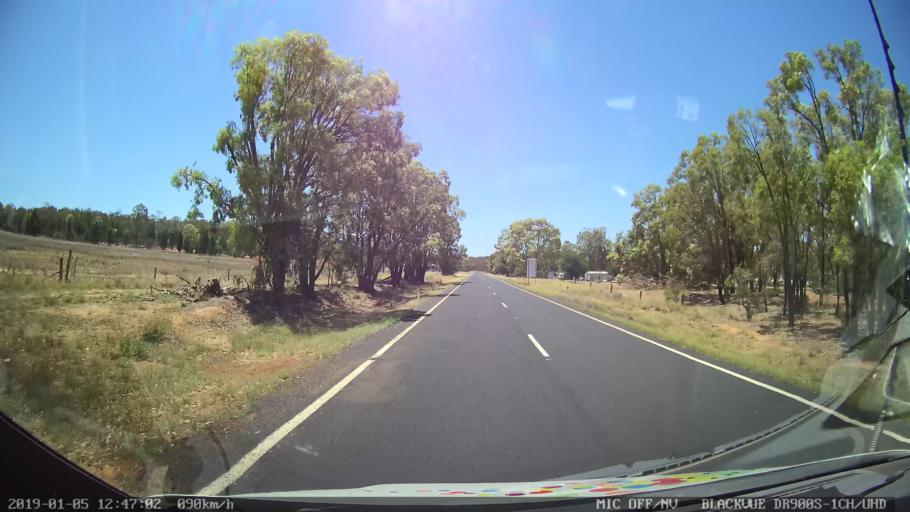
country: AU
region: New South Wales
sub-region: Warrumbungle Shire
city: Coonabarabran
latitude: -31.1156
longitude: 149.5709
